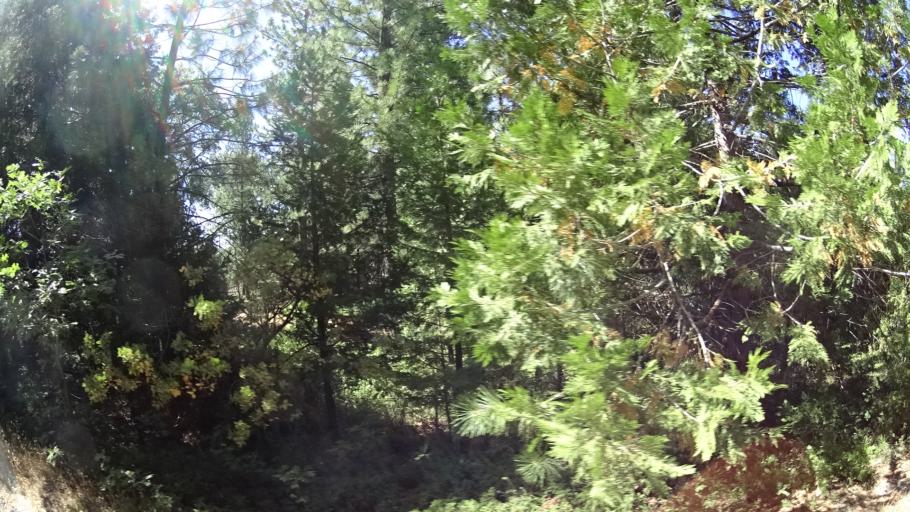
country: US
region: California
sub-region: Amador County
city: Pioneer
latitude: 38.3992
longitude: -120.4655
